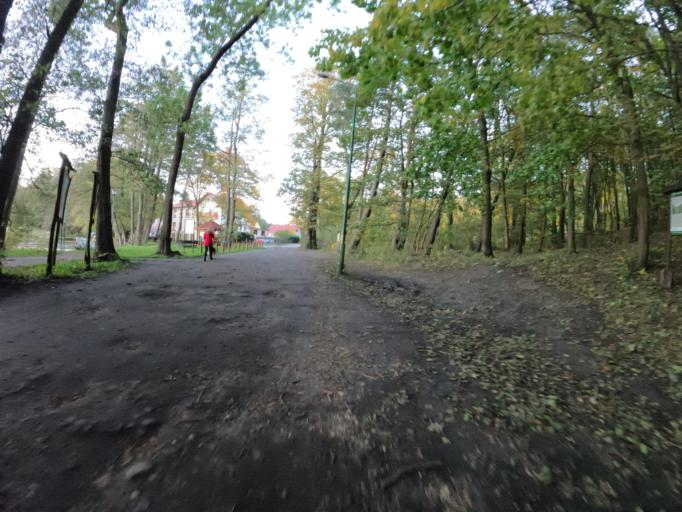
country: PL
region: West Pomeranian Voivodeship
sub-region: Powiat mysliborski
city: Barlinek
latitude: 52.9831
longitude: 15.2300
